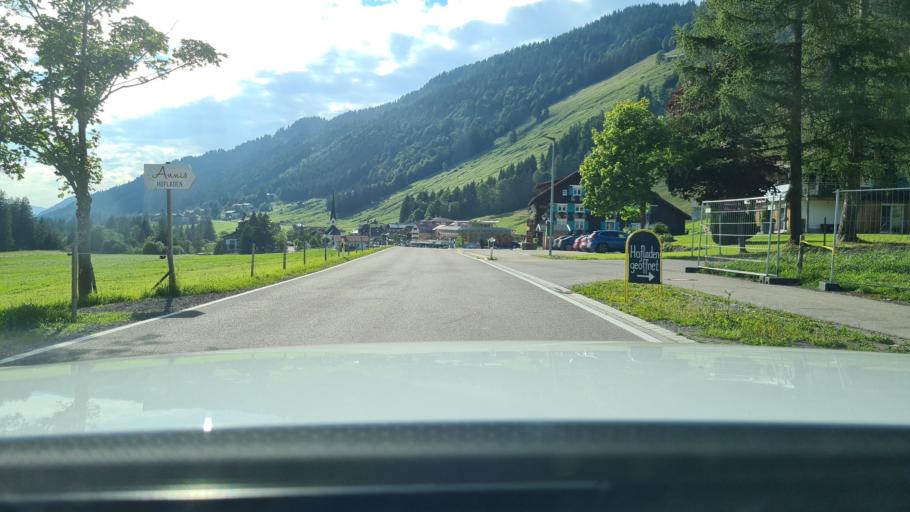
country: DE
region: Bavaria
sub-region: Swabia
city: Balderschwang
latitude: 47.4652
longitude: 10.1107
